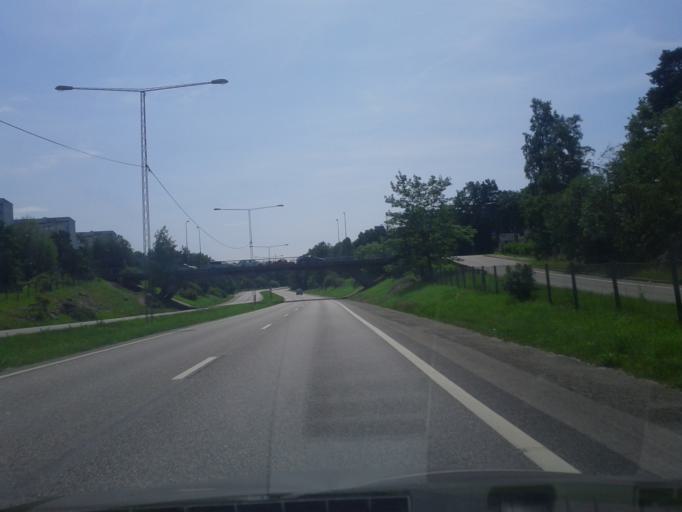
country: SE
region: Stockholm
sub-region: Huddinge Kommun
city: Huddinge
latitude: 59.2611
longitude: 18.0099
